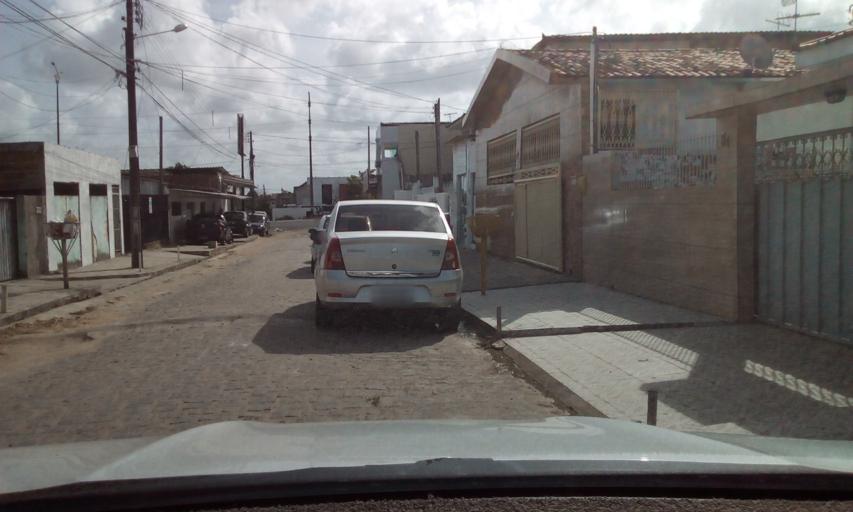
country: BR
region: Paraiba
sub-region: Joao Pessoa
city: Joao Pessoa
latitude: -7.1683
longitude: -34.8556
